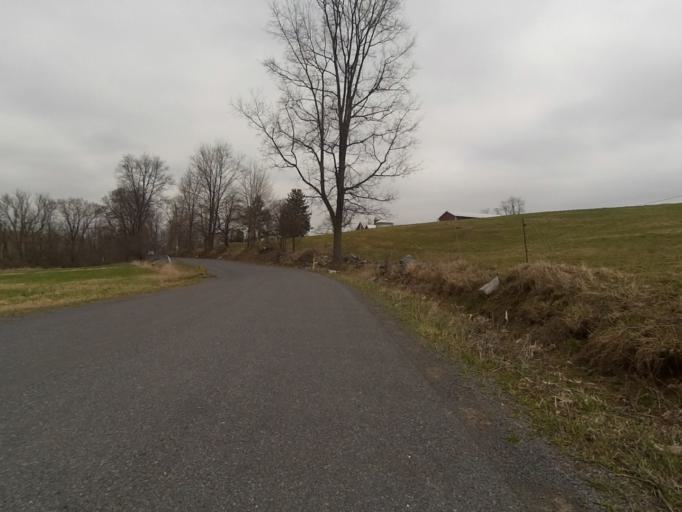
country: US
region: Pennsylvania
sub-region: Centre County
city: Boalsburg
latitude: 40.7917
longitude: -77.7840
